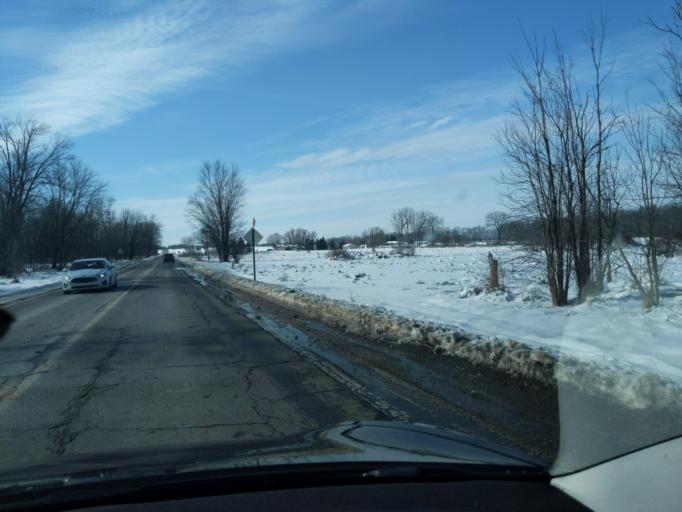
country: US
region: Michigan
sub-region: Livingston County
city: Fowlerville
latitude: 42.5993
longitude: -84.0731
